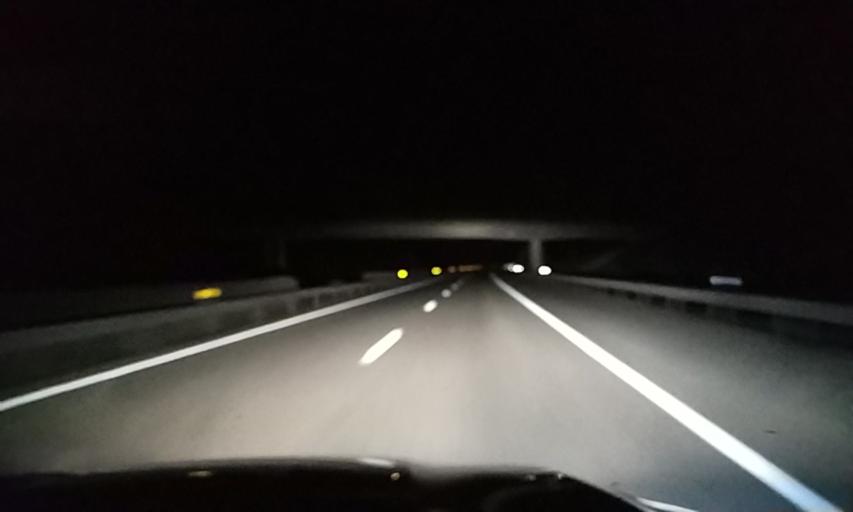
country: PT
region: Santarem
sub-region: Ourem
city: Fatima
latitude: 39.5955
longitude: -8.6681
